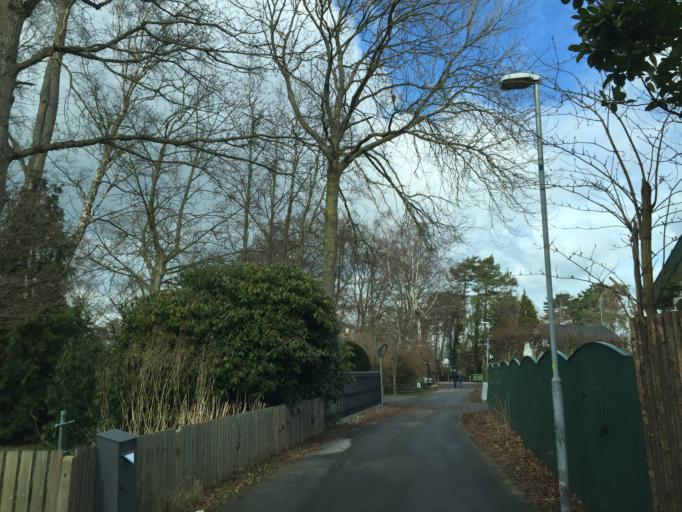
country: SE
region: Skane
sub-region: Vellinge Kommun
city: Skanor med Falsterbo
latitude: 55.3959
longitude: 12.8322
